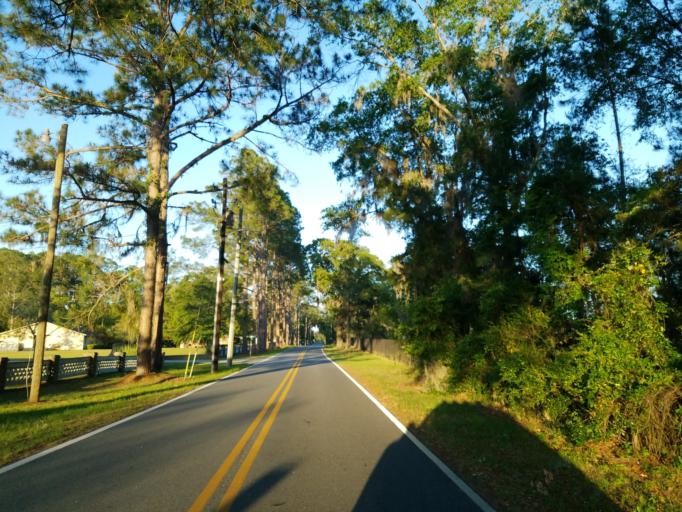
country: US
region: Georgia
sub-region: Lowndes County
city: Valdosta
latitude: 30.7502
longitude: -83.2255
